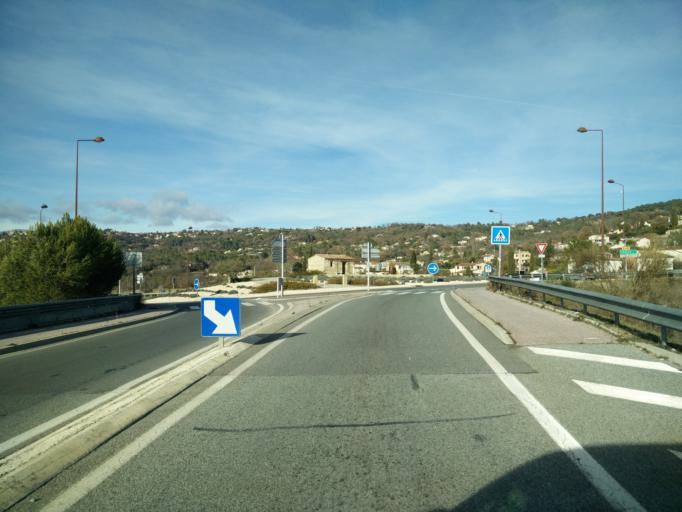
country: FR
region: Provence-Alpes-Cote d'Azur
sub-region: Departement du Var
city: Montauroux
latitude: 43.5985
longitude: 6.7861
